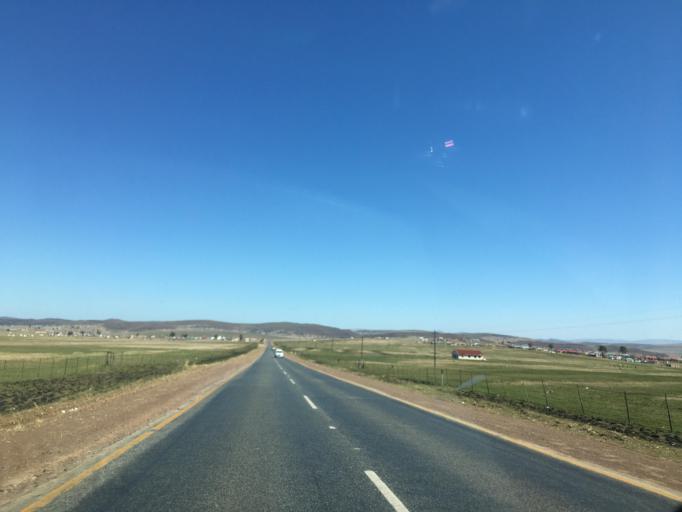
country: ZA
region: Eastern Cape
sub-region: Chris Hani District Municipality
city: Cofimvaba
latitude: -31.9452
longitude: 27.8347
